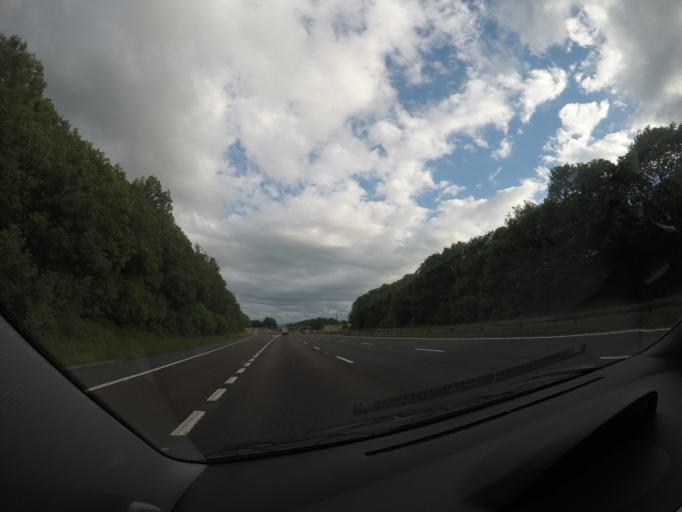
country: GB
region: England
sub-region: Cumbria
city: Penrith
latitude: 54.6975
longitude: -2.7911
